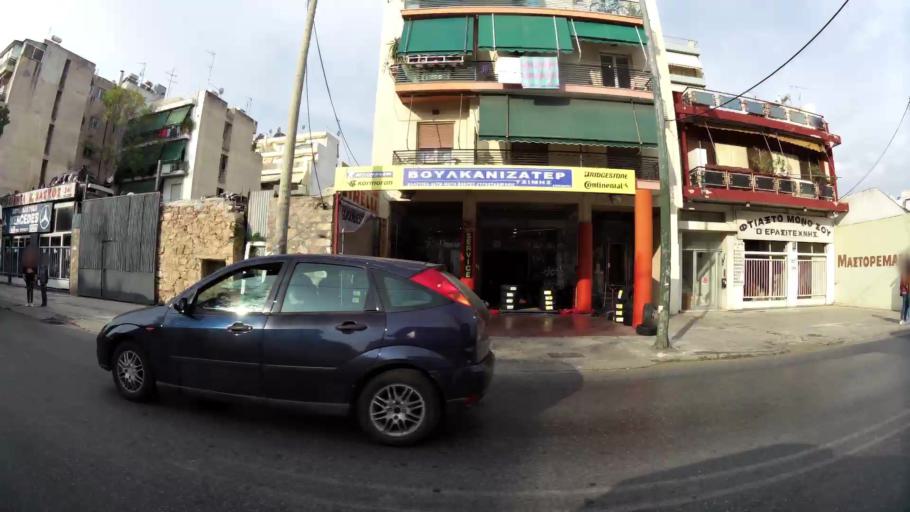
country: GR
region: Attica
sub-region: Nomarchia Athinas
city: Kipseli
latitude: 38.0064
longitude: 23.7223
